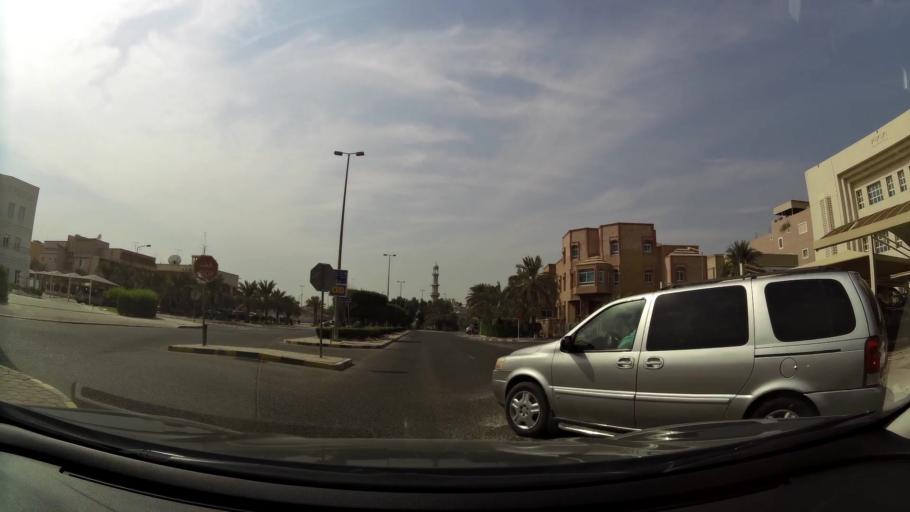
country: KW
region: Al Asimah
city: Ash Shamiyah
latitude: 29.3403
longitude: 47.9741
